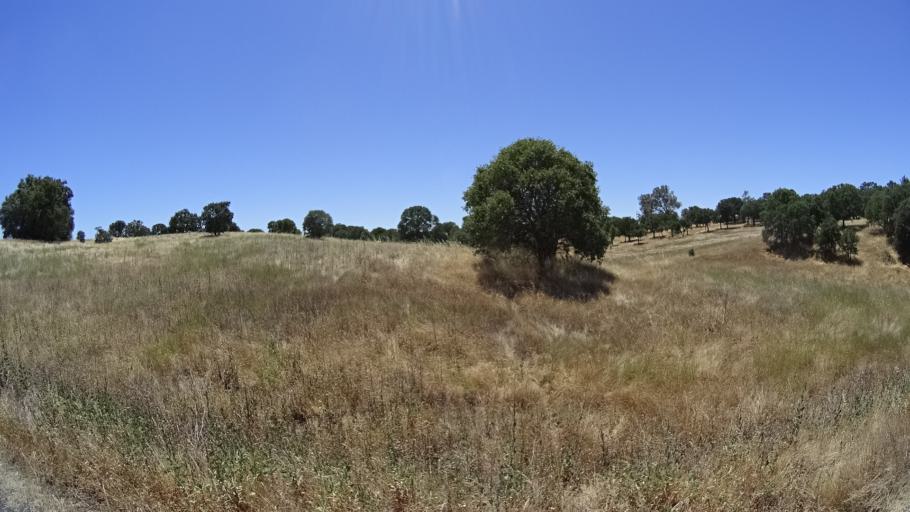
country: US
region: California
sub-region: Calaveras County
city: Copperopolis
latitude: 37.9783
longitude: -120.6750
